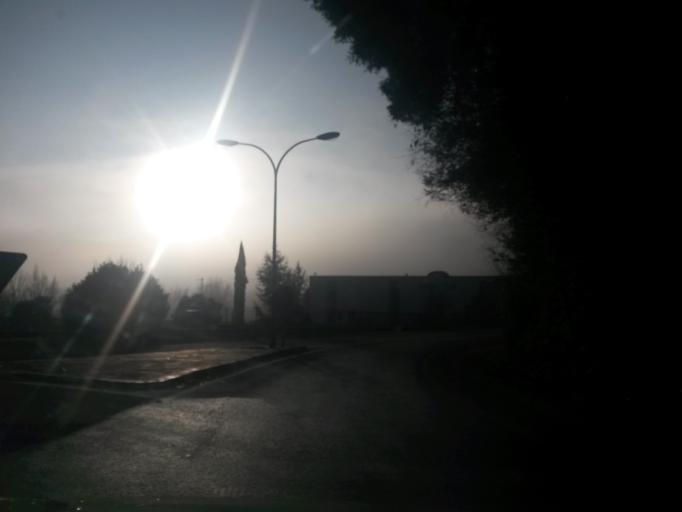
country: ES
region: Catalonia
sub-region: Provincia de Girona
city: Argelaguer
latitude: 42.2131
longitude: 2.6091
